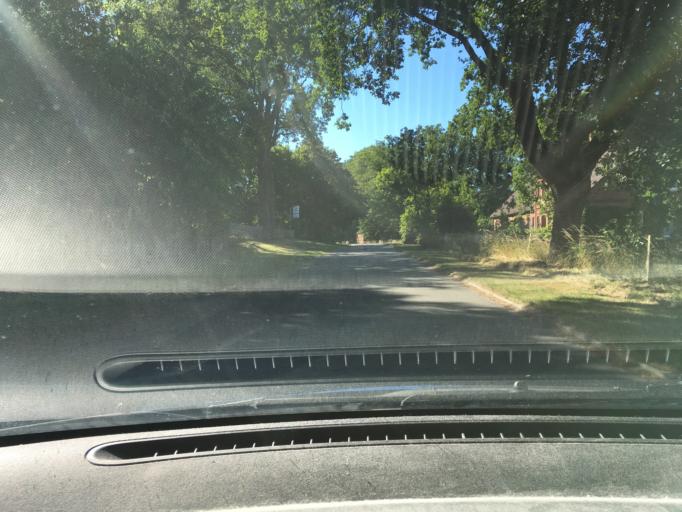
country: DE
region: Lower Saxony
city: Altenmedingen
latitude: 53.1782
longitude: 10.6325
